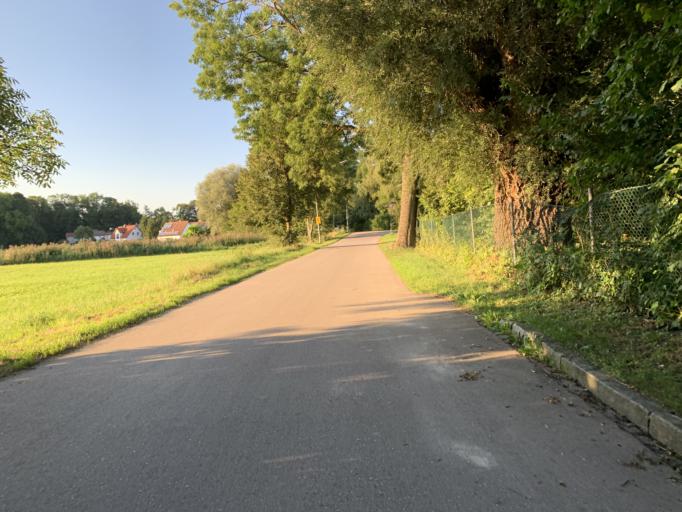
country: DE
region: Bavaria
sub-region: Upper Bavaria
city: Freising
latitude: 48.3831
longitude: 11.7509
